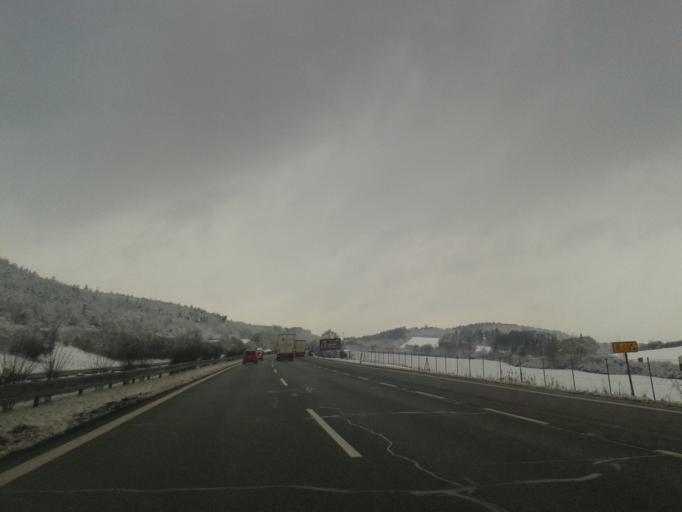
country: CZ
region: Central Bohemia
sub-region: Okres Beroun
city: Lodenice
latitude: 50.0058
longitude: 14.1741
